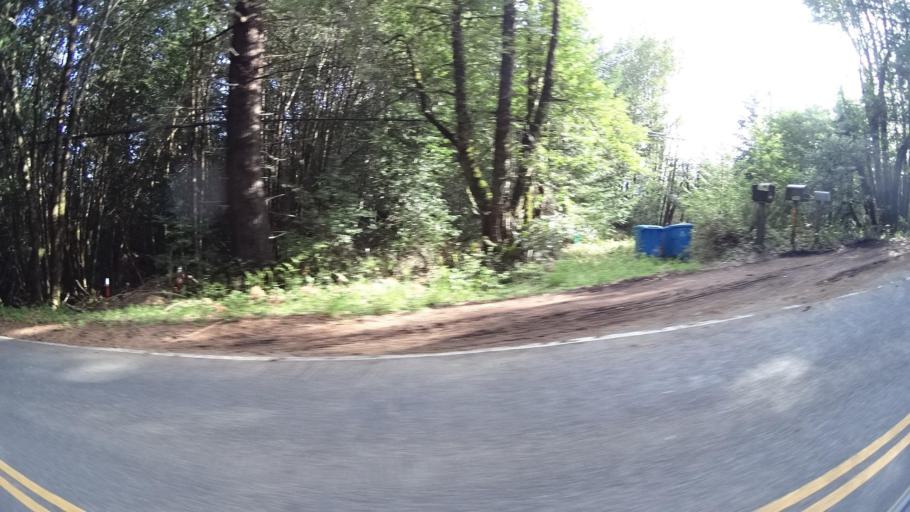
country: US
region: California
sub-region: Humboldt County
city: Blue Lake
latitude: 40.7400
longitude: -123.9525
